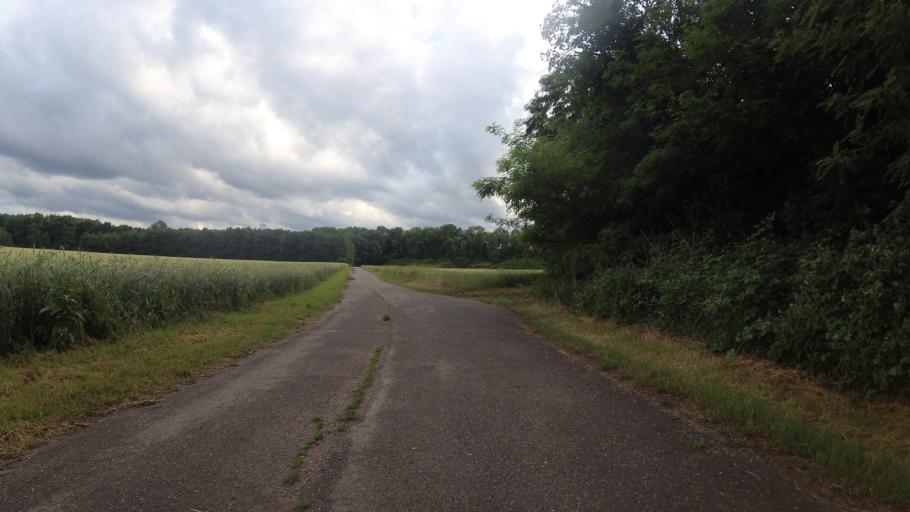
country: DE
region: Baden-Wuerttemberg
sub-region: Freiburg Region
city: Weil am Rhein
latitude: 47.5810
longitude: 7.6129
